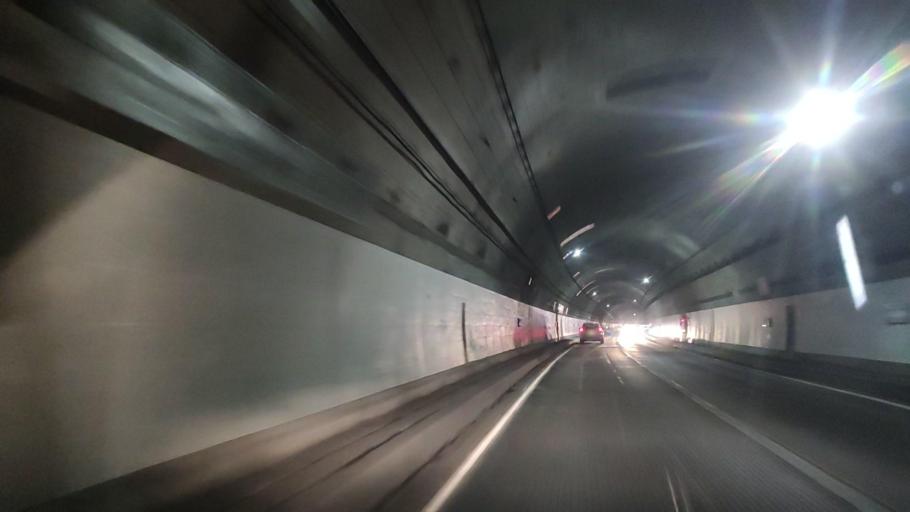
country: JP
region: Hokkaido
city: Rumoi
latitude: 43.7028
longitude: 141.3365
